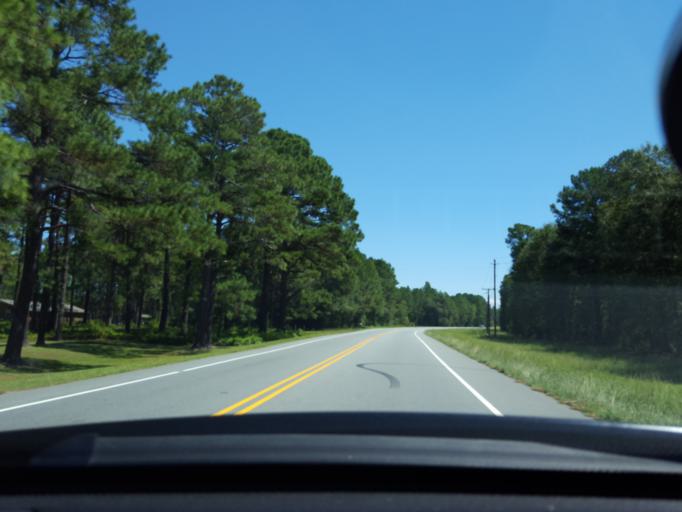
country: US
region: North Carolina
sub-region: Bladen County
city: Elizabethtown
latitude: 34.6496
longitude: -78.5438
